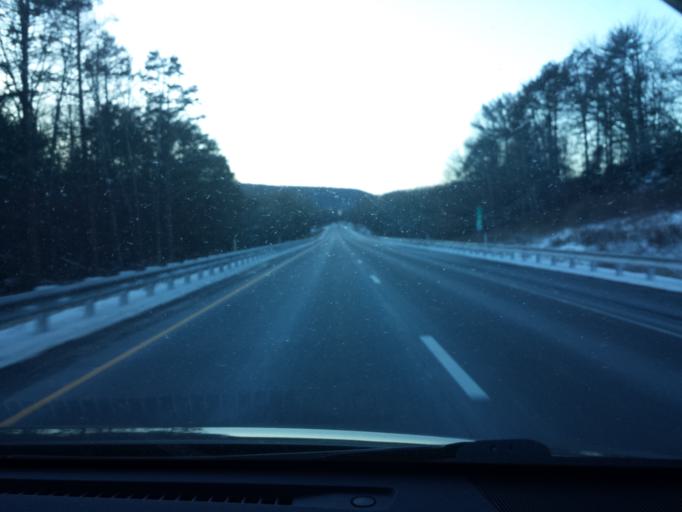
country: US
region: Pennsylvania
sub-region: Clinton County
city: Castanea
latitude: 41.0486
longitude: -77.3268
